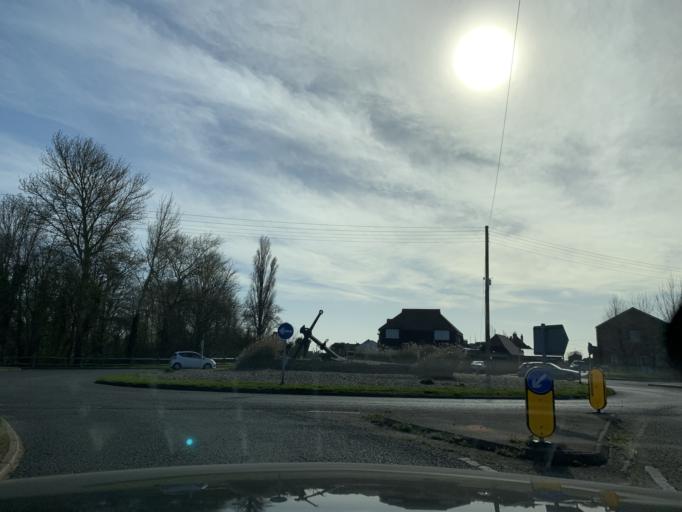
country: GB
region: England
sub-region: Kent
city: Lydd
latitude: 50.9517
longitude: 0.9125
